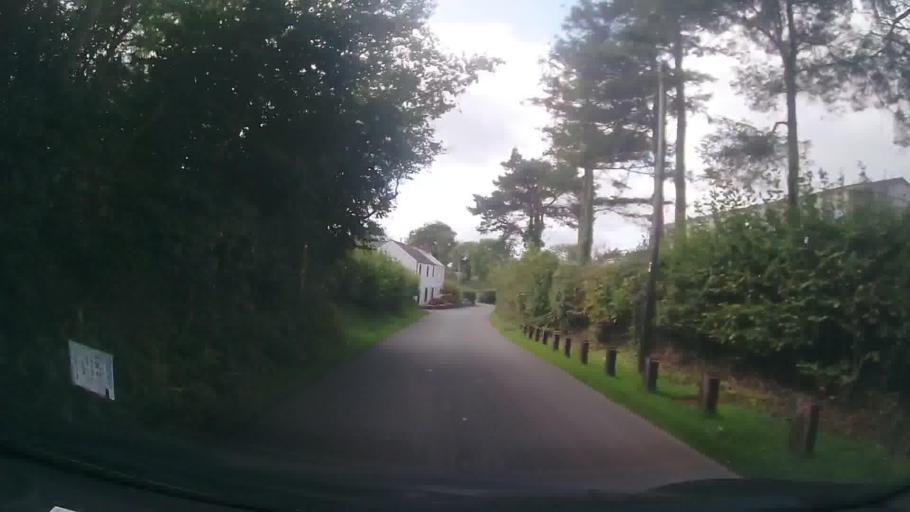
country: GB
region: Wales
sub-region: Pembrokeshire
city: Saundersfoot
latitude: 51.7515
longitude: -4.6530
